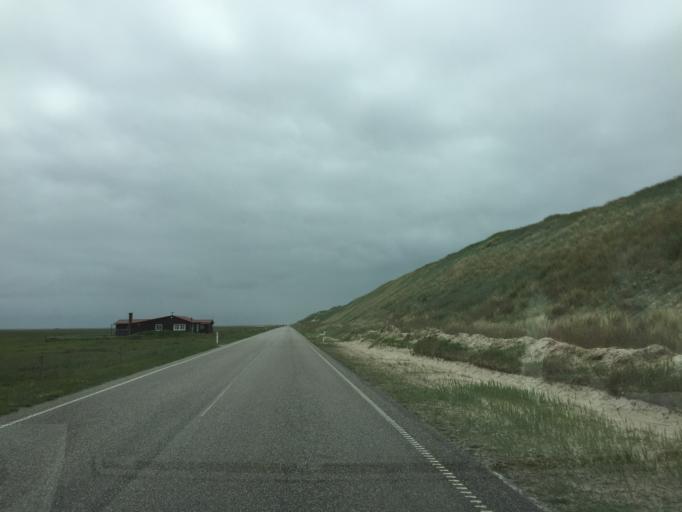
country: DK
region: Central Jutland
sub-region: Lemvig Kommune
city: Harboore
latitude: 56.4410
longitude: 8.1248
